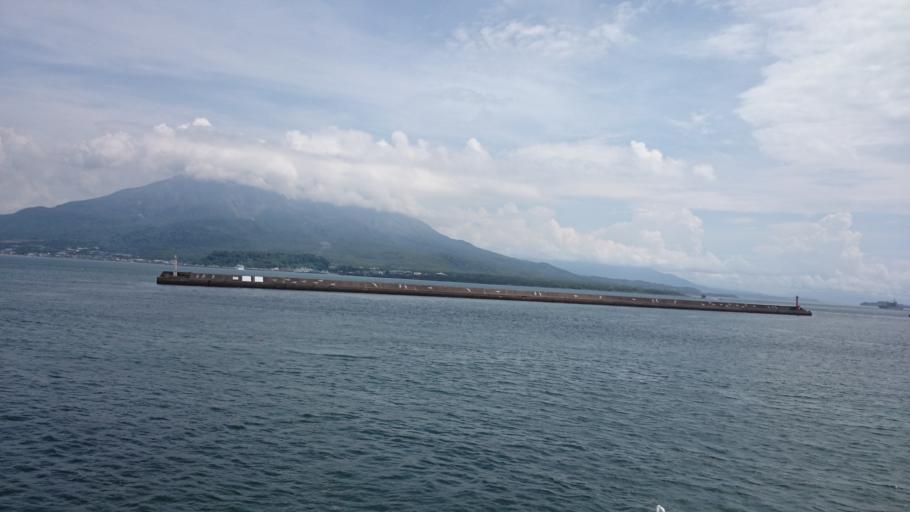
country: JP
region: Kagoshima
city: Kagoshima-shi
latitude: 31.5979
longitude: 130.5686
